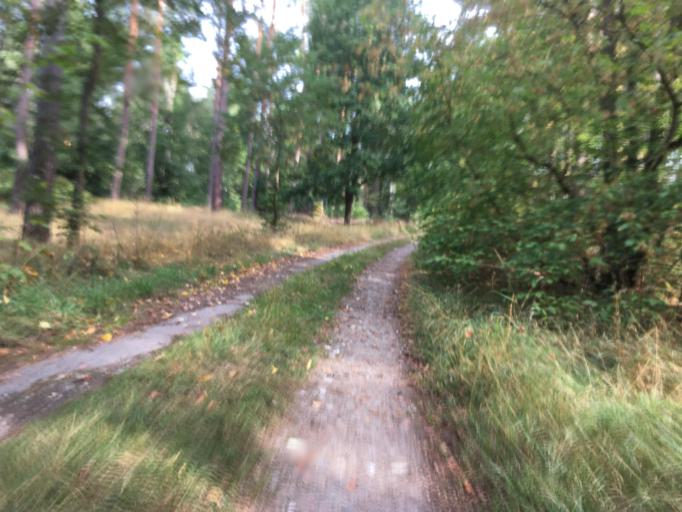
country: DE
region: Brandenburg
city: Marienwerder
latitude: 52.9694
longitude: 13.5307
